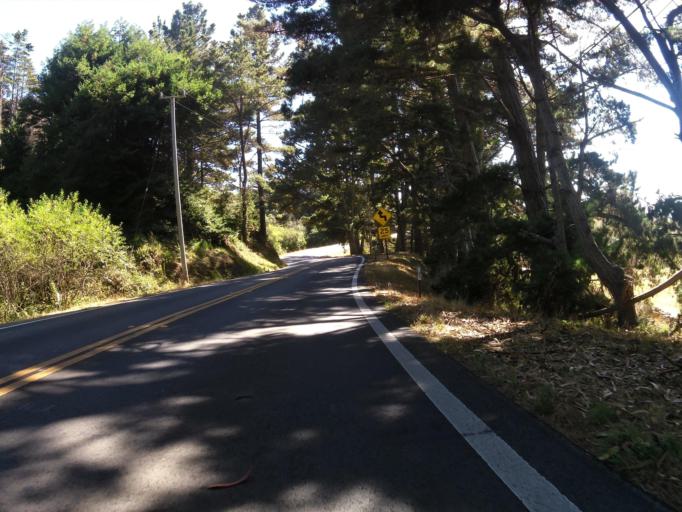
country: US
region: California
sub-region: Mendocino County
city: Fort Bragg
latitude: 39.6272
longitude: -123.7825
